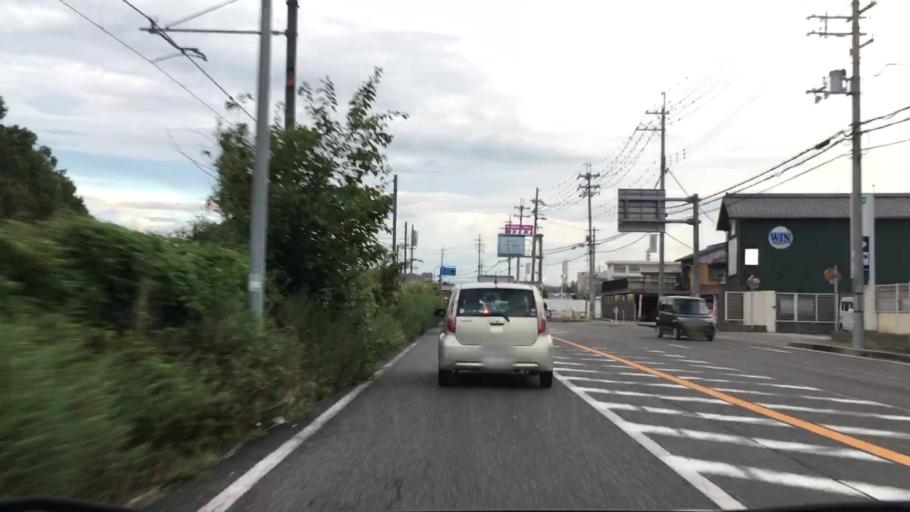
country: JP
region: Hyogo
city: Himeji
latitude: 34.8730
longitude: 134.7294
